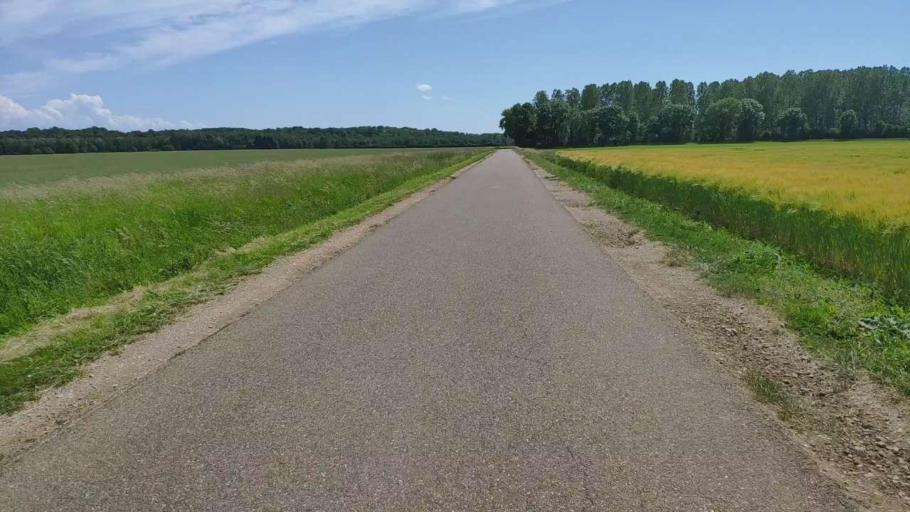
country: FR
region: Franche-Comte
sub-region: Departement du Jura
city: Bletterans
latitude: 46.7331
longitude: 5.4823
